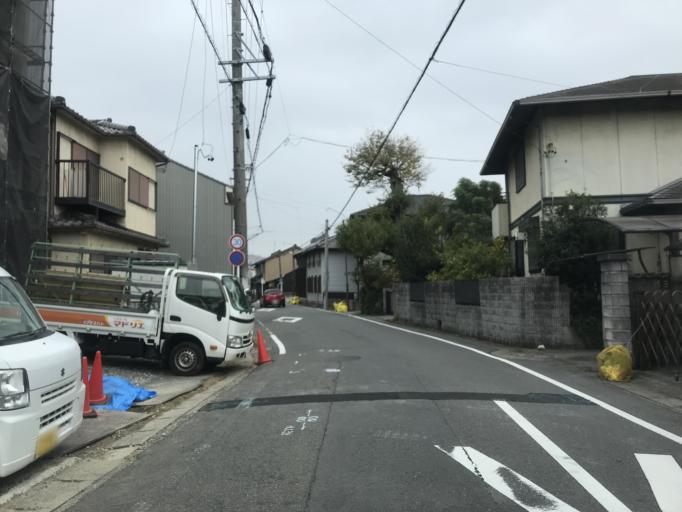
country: JP
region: Aichi
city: Nagoya-shi
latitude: 35.1990
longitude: 136.8425
